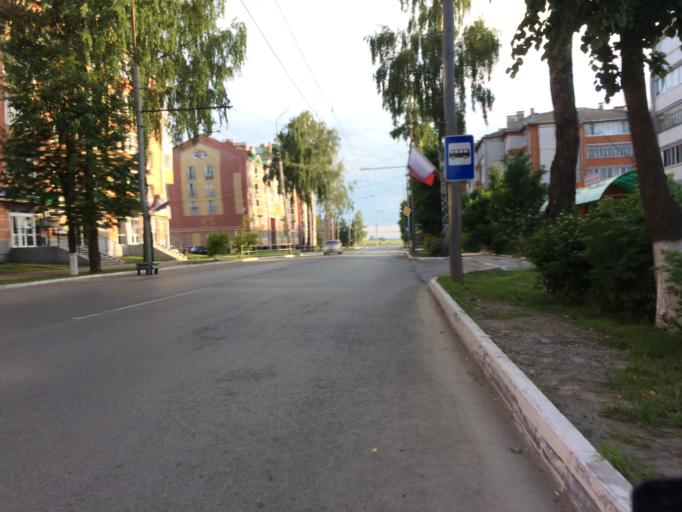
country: RU
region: Mariy-El
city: Medvedevo
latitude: 56.6371
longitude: 47.8030
